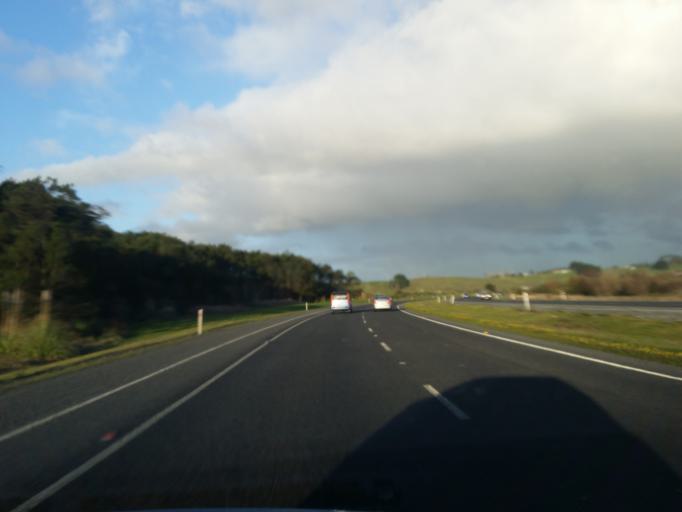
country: NZ
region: Waikato
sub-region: Waikato District
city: Te Kauwhata
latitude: -37.3471
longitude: 175.0741
